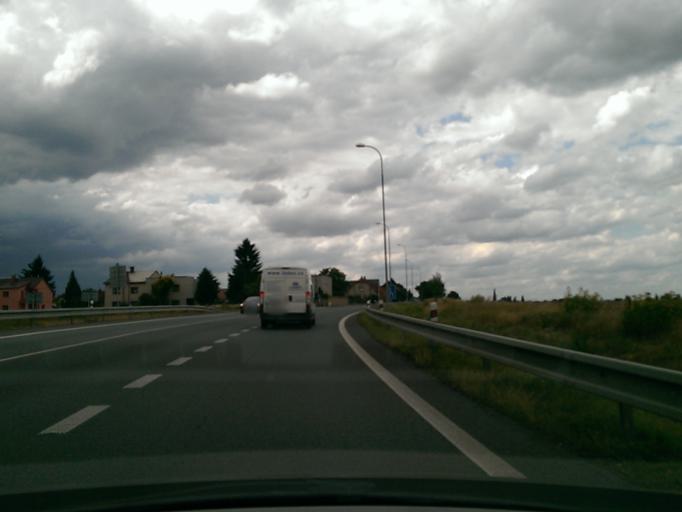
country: CZ
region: Central Bohemia
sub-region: Okres Nymburk
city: Nymburk
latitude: 50.2054
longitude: 15.0356
